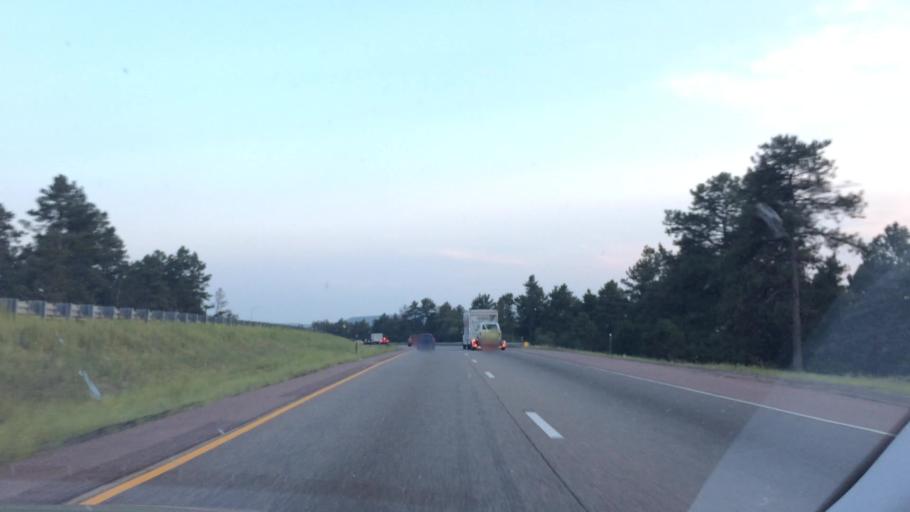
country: US
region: Colorado
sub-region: El Paso County
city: Palmer Lake
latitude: 39.2229
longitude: -104.8788
